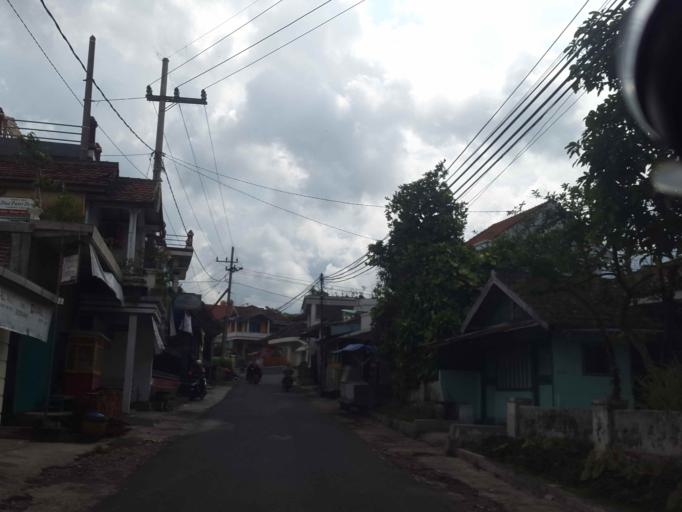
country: ID
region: East Java
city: Batu
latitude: -7.8915
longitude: 112.5484
